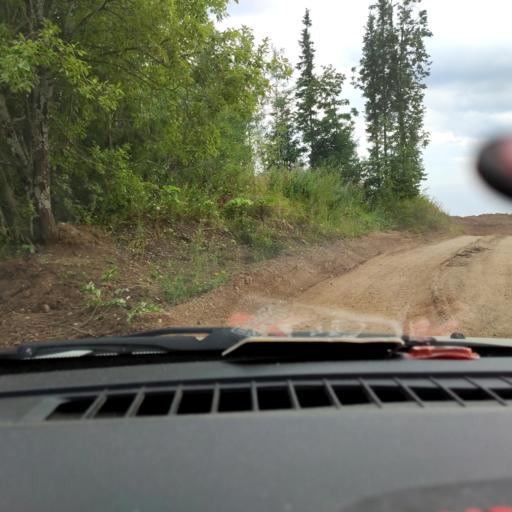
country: RU
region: Perm
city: Kultayevo
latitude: 57.8052
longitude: 56.0035
